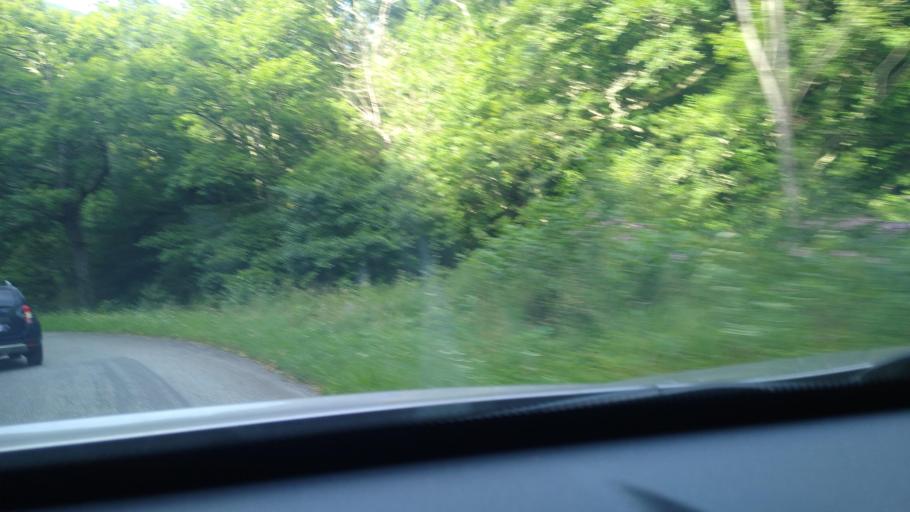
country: FR
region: Midi-Pyrenees
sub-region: Departement de l'Ariege
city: Saint-Girons
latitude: 42.7924
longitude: 1.1888
